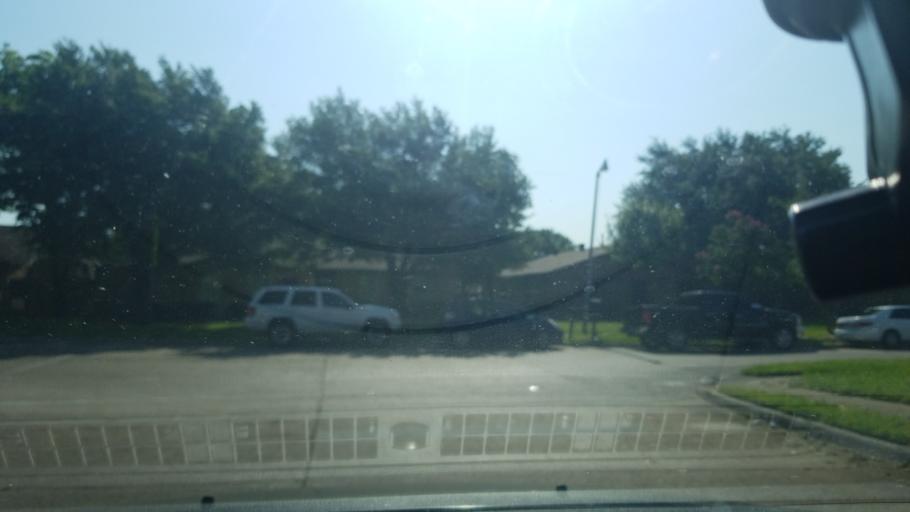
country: US
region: Texas
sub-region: Dallas County
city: Mesquite
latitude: 32.8288
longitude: -96.6353
